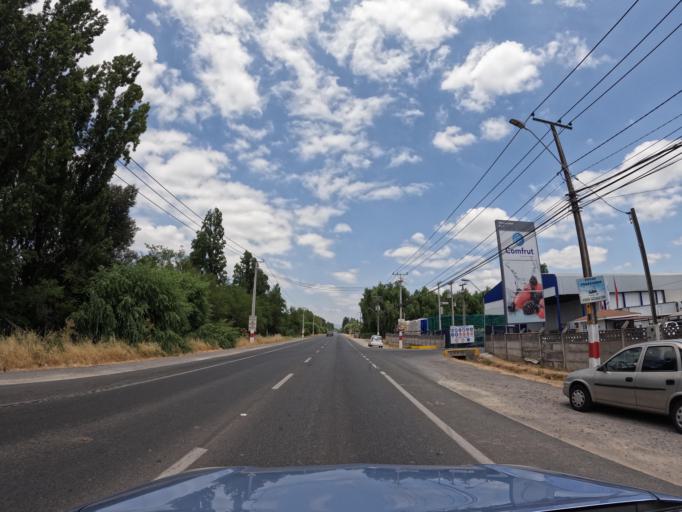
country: CL
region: Maule
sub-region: Provincia de Curico
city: Curico
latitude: -35.0069
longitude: -71.2229
